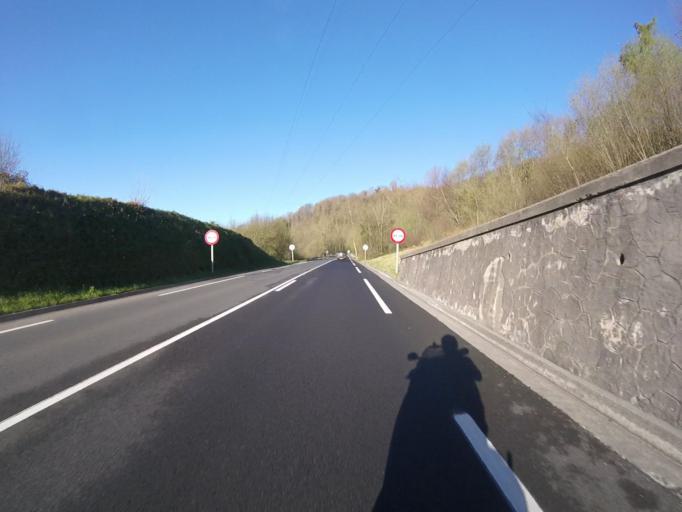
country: ES
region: Basque Country
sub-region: Provincia de Guipuzcoa
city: Errenteria
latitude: 43.2851
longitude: -1.9097
